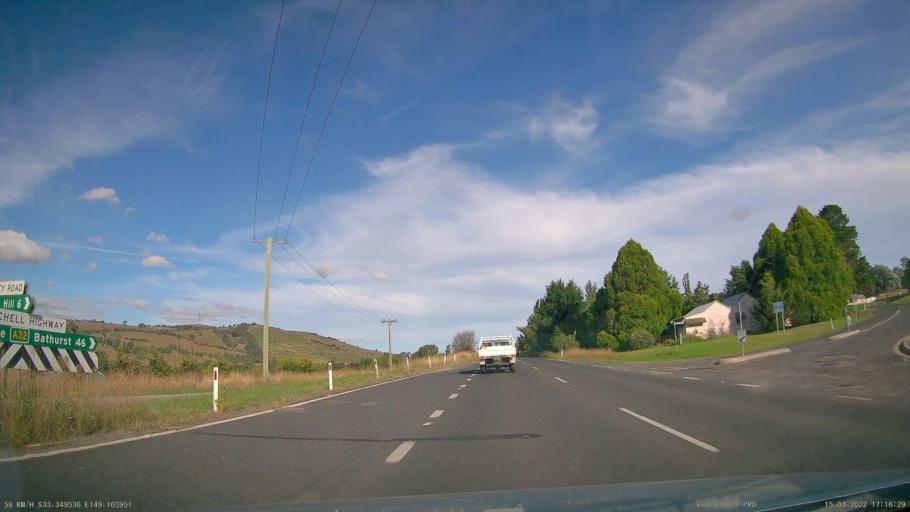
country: AU
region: New South Wales
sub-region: Orange Municipality
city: Orange
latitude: -33.3497
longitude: 149.1661
